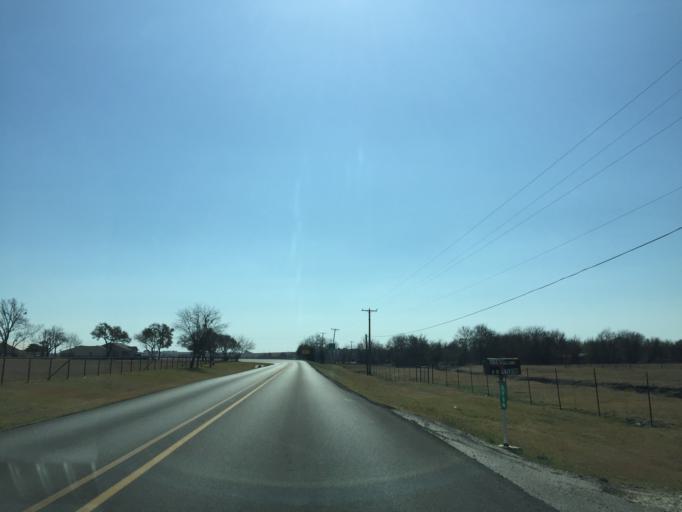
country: US
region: Texas
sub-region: Williamson County
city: Serenada
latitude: 30.7339
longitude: -97.5956
